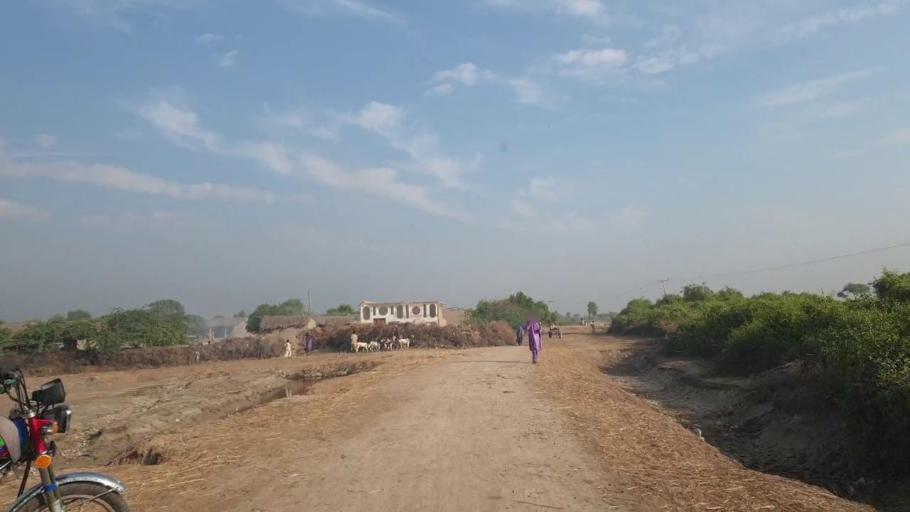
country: PK
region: Sindh
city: Tando Bago
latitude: 24.8249
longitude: 68.9740
